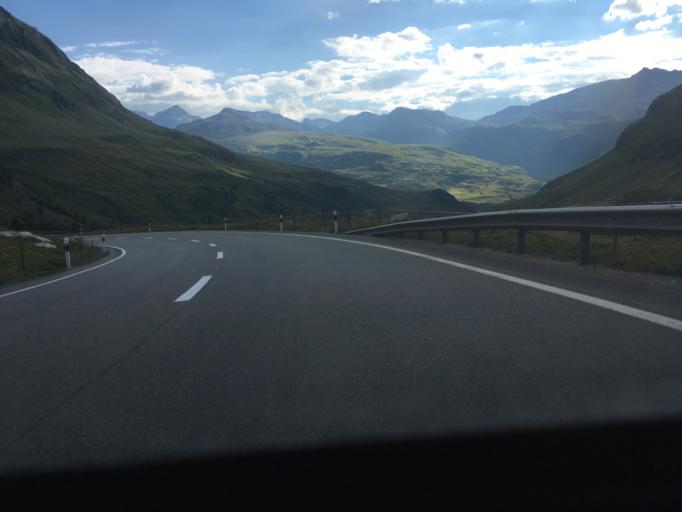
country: CH
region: Grisons
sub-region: Maloja District
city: Silvaplana
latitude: 46.4662
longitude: 9.6906
